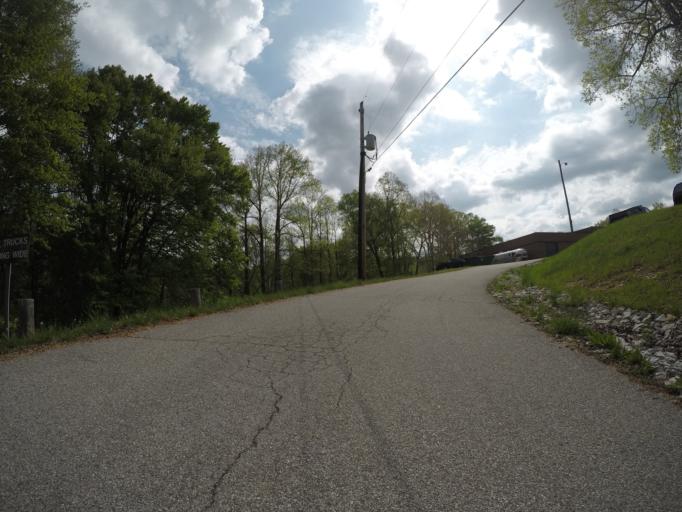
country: US
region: West Virginia
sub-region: Kanawha County
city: Alum Creek
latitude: 38.2672
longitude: -81.7926
